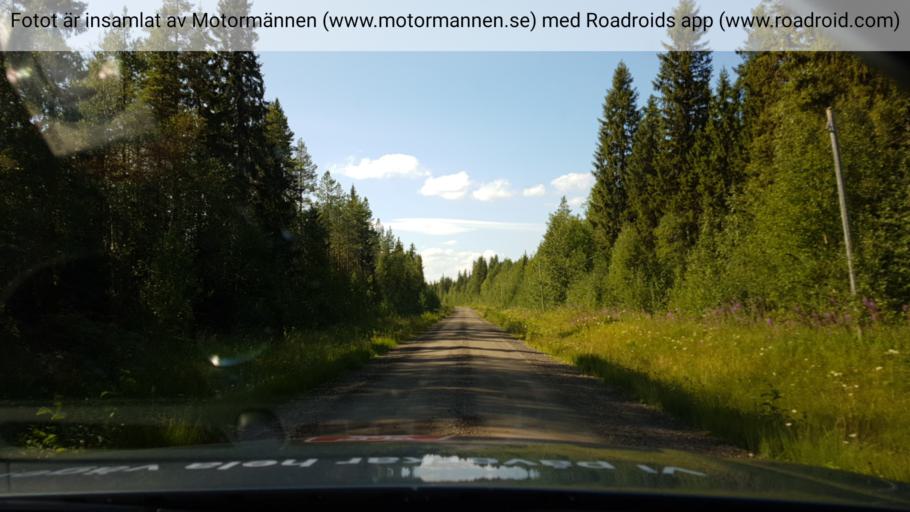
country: SE
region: Vaesterbotten
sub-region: Dorotea Kommun
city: Dorotea
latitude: 64.0944
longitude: 16.4530
